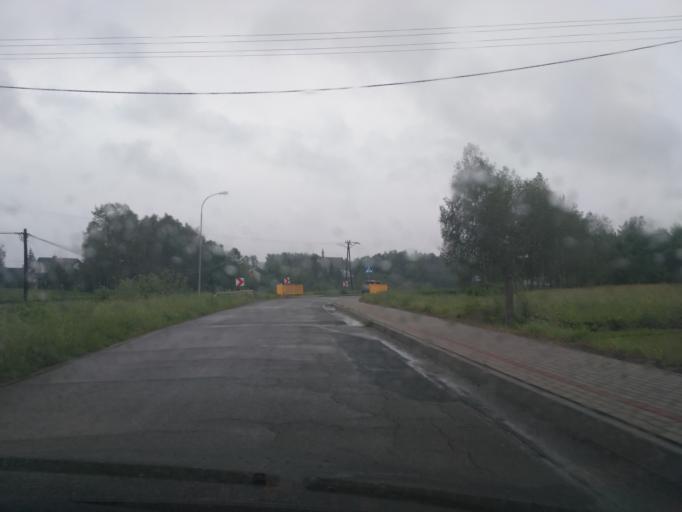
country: PL
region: Subcarpathian Voivodeship
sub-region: Powiat krosnienski
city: Leki
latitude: 49.7909
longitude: 21.6518
